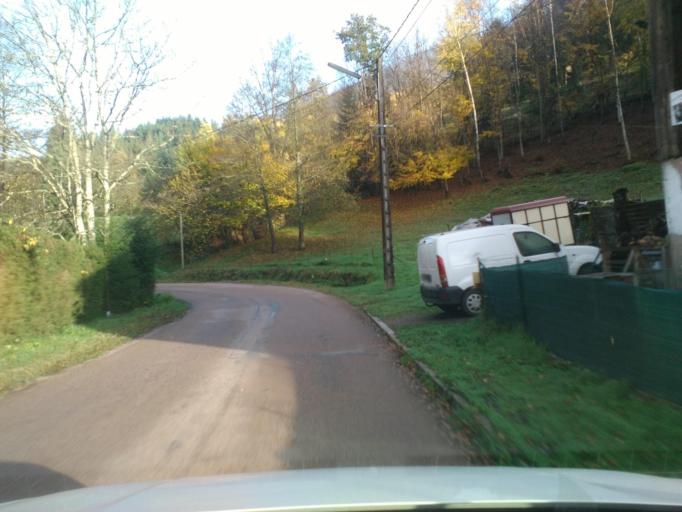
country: FR
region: Lorraine
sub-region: Departement des Vosges
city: Senones
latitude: 48.4229
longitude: 7.0383
